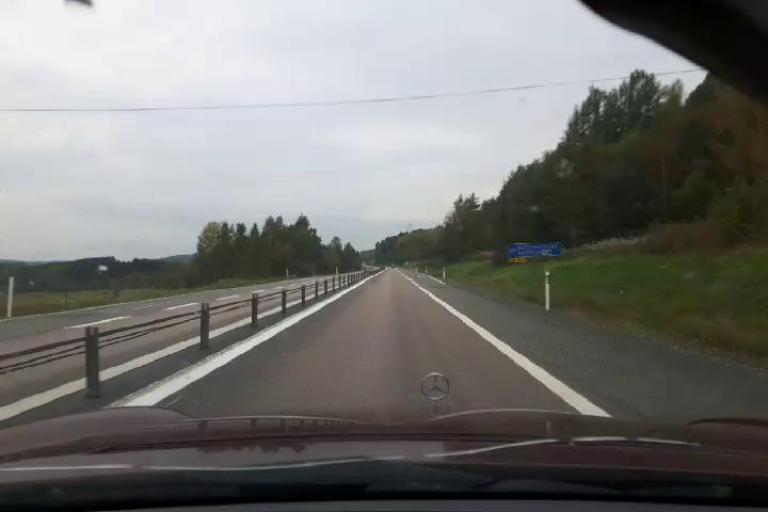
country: SE
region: Vaesternorrland
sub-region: Haernoesands Kommun
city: Haernoesand
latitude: 62.8542
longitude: 18.0132
